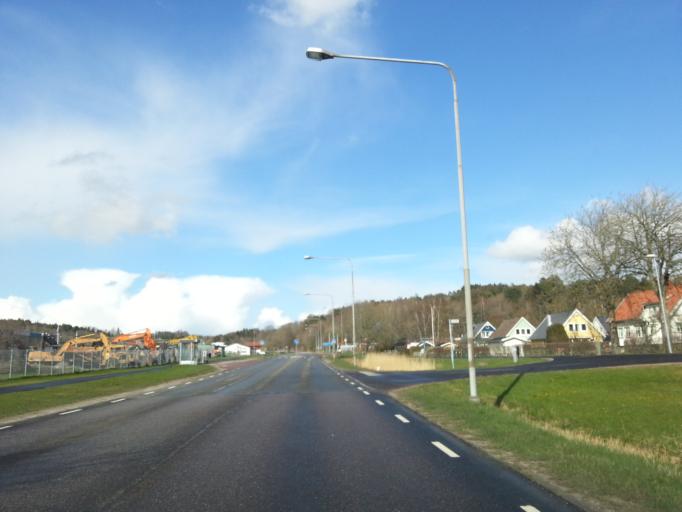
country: SE
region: Vaestra Goetaland
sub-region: Kungalvs Kommun
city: Kungalv
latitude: 57.8837
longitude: 11.9879
